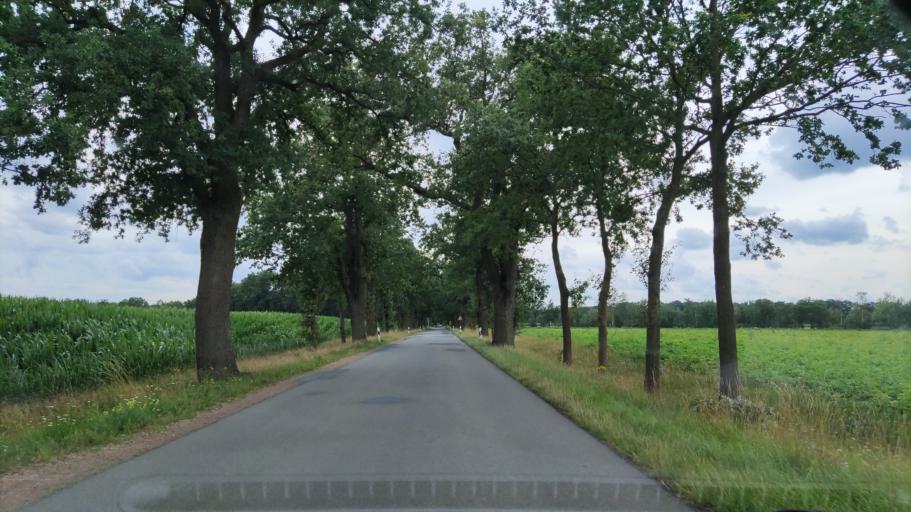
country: DE
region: Lower Saxony
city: Dannenberg
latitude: 53.0761
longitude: 11.1292
